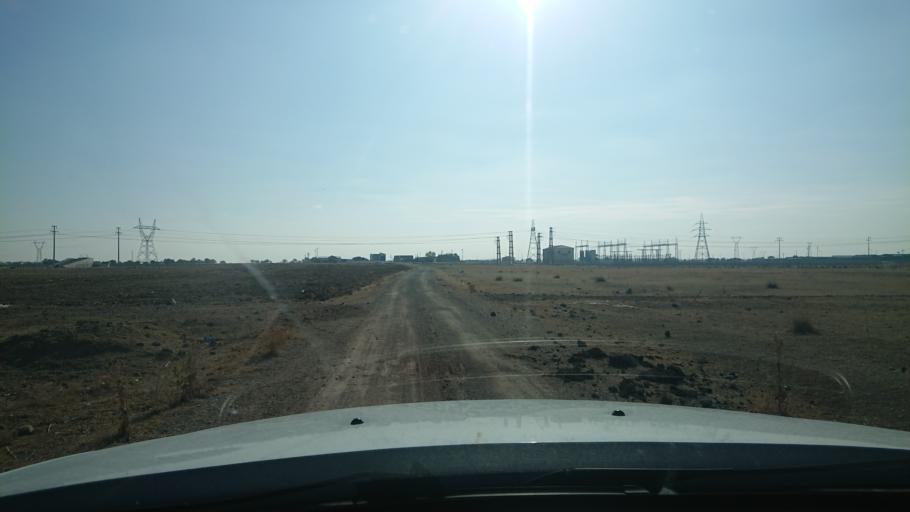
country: TR
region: Aksaray
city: Sultanhani
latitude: 38.2563
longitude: 33.4716
